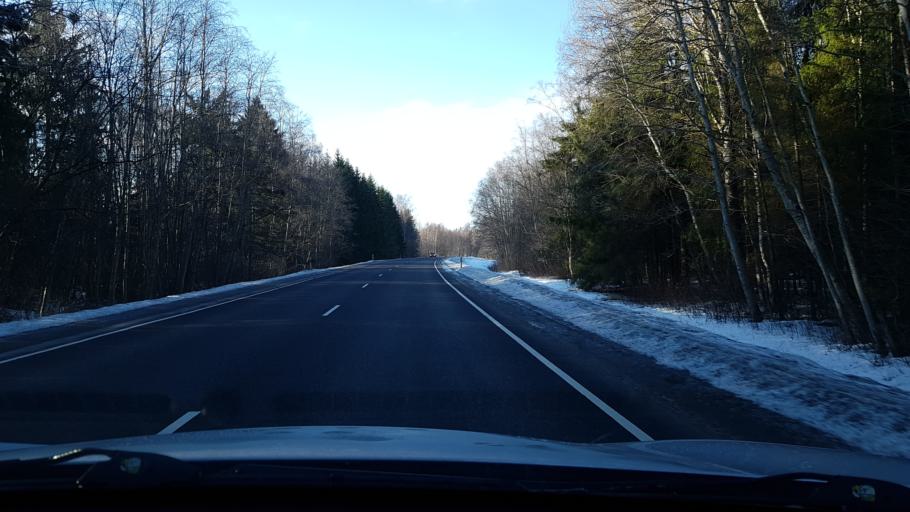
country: EE
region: Viljandimaa
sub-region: Vohma linn
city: Vohma
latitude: 58.7027
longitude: 25.7376
